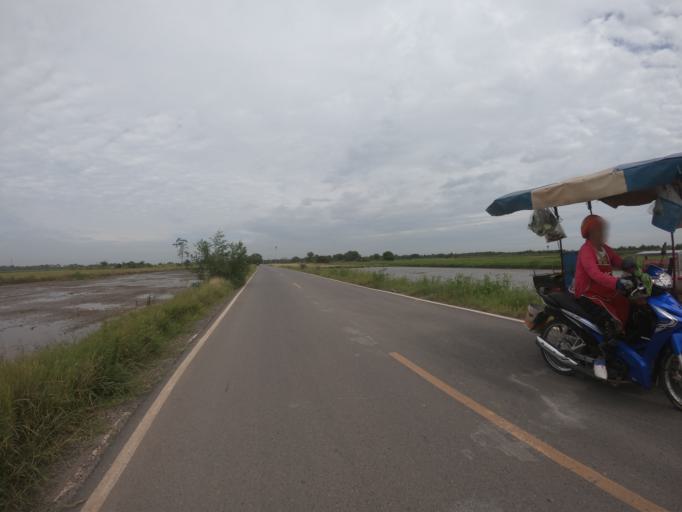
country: TH
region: Pathum Thani
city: Nong Suea
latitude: 14.0338
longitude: 100.8792
